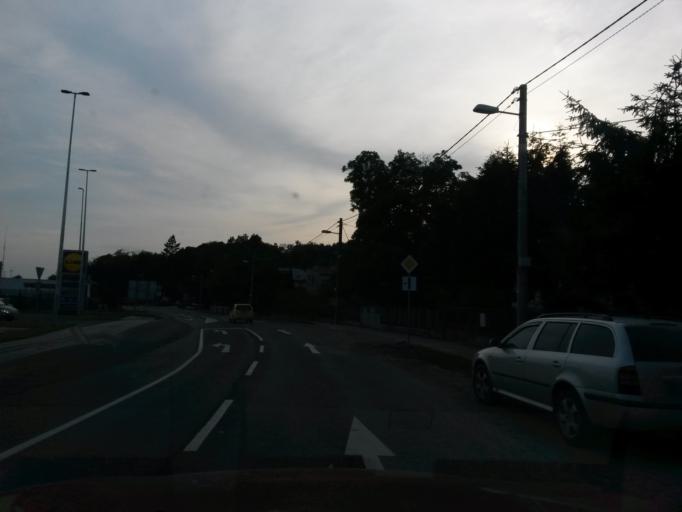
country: SK
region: Kosicky
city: Moldava nad Bodvou
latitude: 48.6099
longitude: 20.9944
